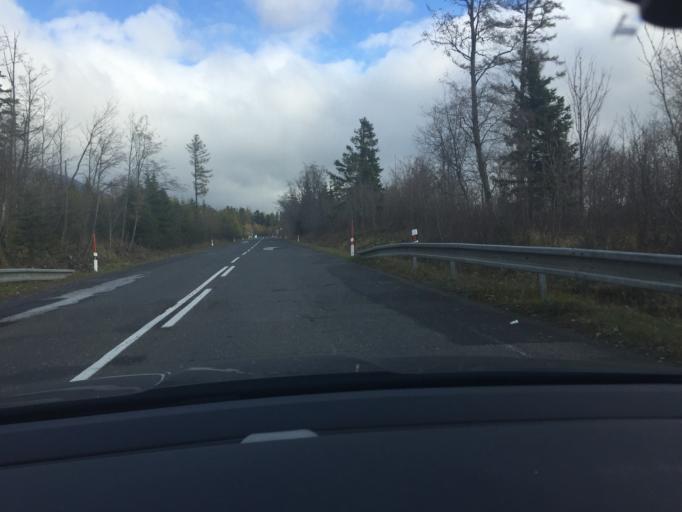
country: SK
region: Presovsky
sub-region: Okres Poprad
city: Nova Lesna
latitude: 49.1844
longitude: 20.2903
